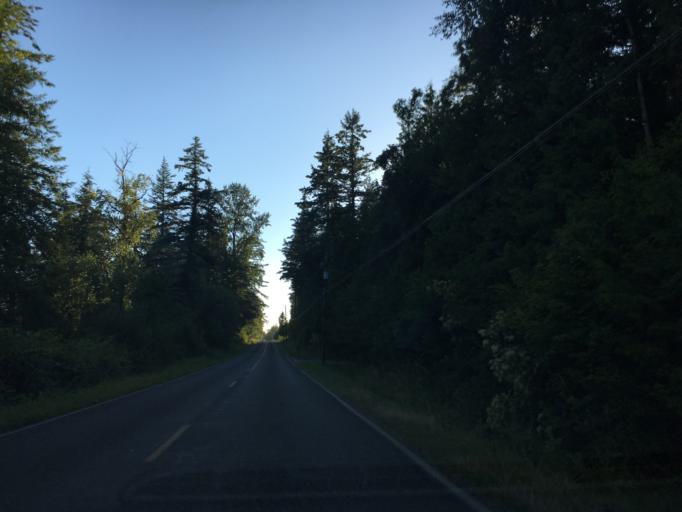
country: US
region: Washington
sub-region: Whatcom County
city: Geneva
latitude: 48.8186
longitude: -122.3851
